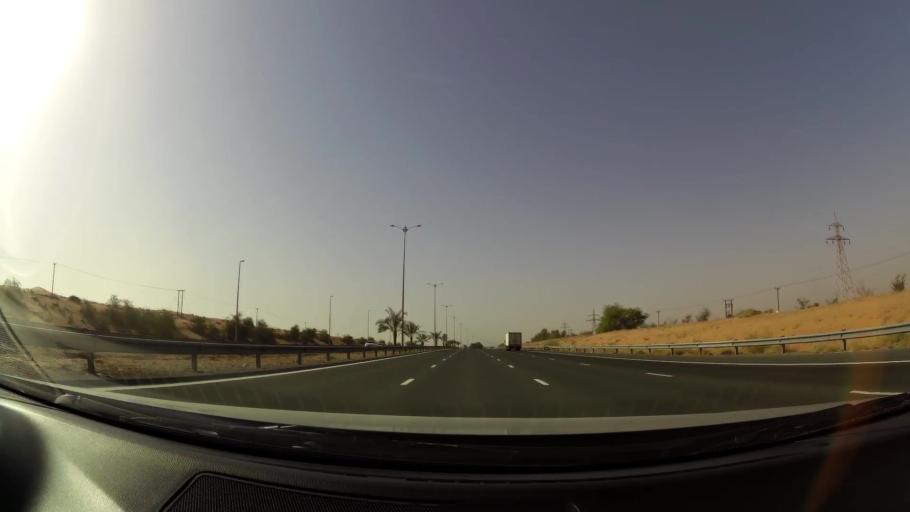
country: OM
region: Al Buraimi
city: Al Buraymi
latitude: 24.6186
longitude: 55.7263
